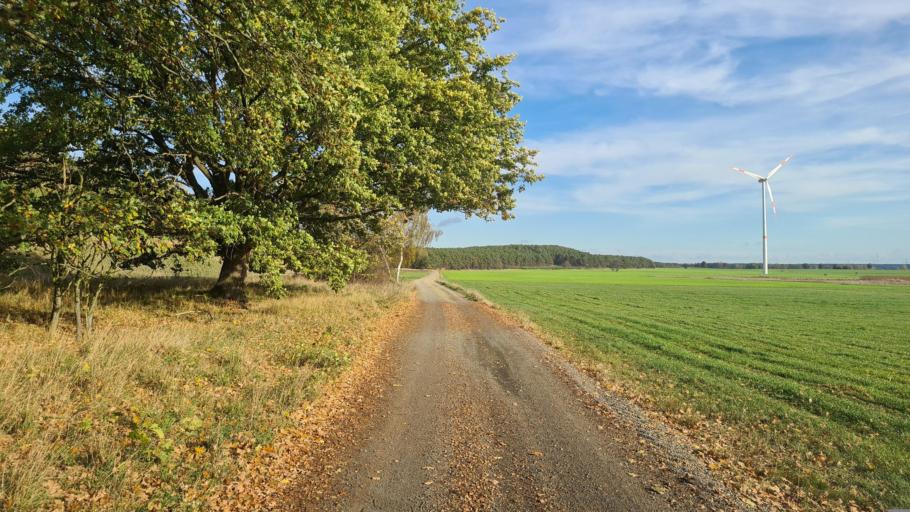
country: DE
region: Brandenburg
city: Schlieben
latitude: 51.7354
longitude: 13.4024
